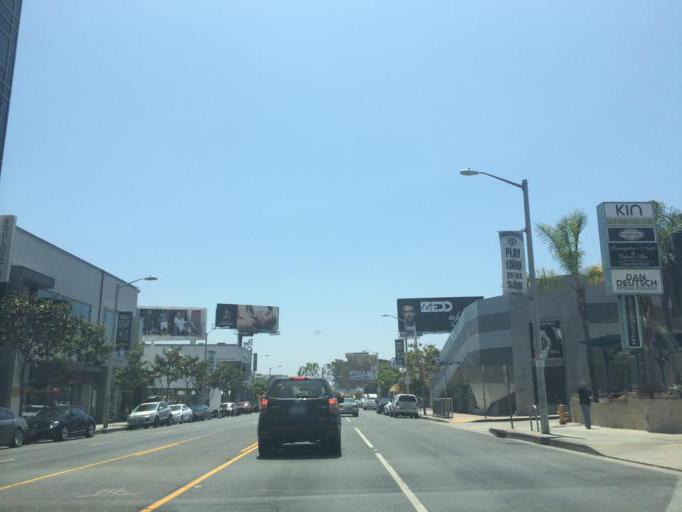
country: US
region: California
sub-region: Los Angeles County
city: West Hollywood
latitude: 34.0933
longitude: -118.3781
